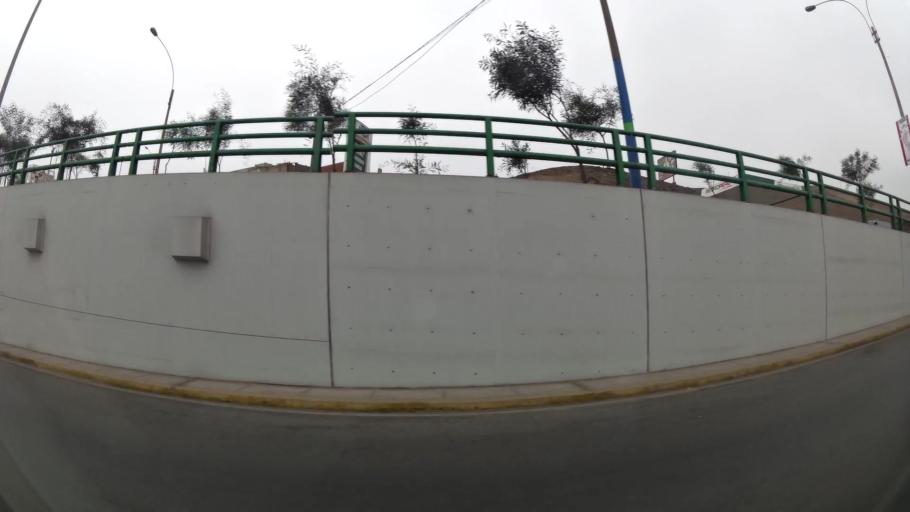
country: PE
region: Lima
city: Ventanilla
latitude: -11.8882
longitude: -77.1260
